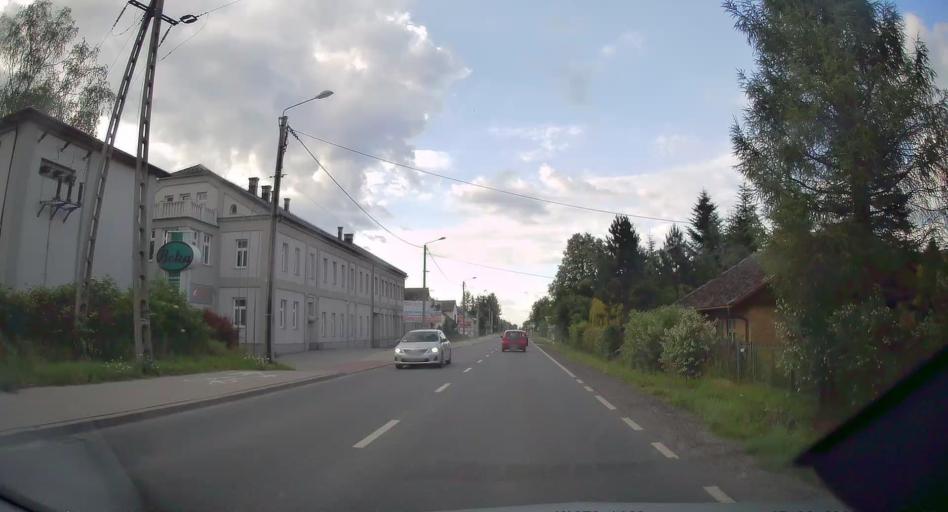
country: PL
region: Lesser Poland Voivodeship
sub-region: Powiat oswiecimski
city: Nowa Wies
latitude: 49.8981
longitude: 19.2182
